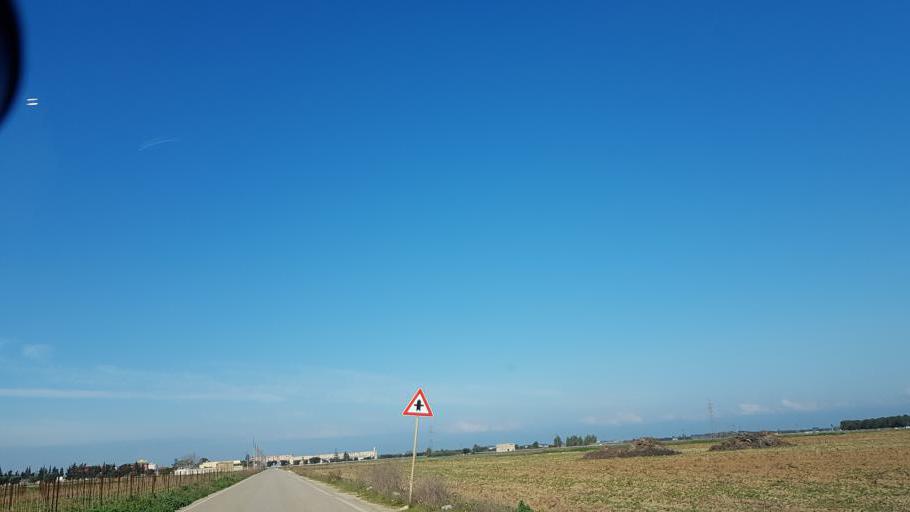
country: IT
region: Apulia
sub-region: Provincia di Brindisi
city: Brindisi
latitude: 40.6035
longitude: 17.8923
